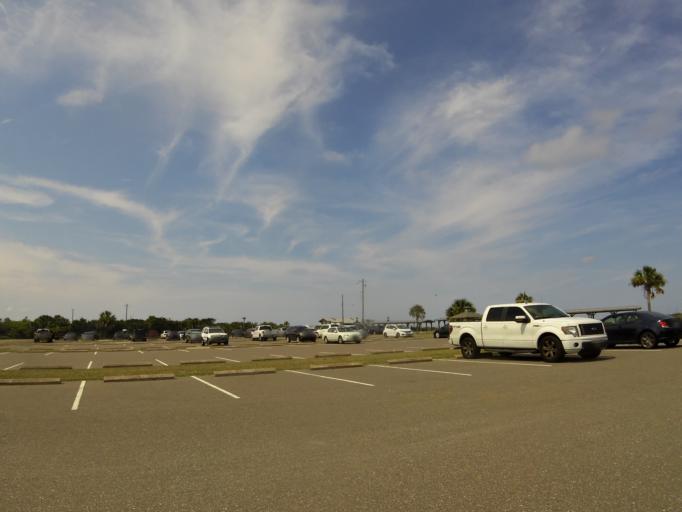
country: US
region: Florida
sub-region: Duval County
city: Atlantic Beach
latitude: 30.4578
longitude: -81.4138
